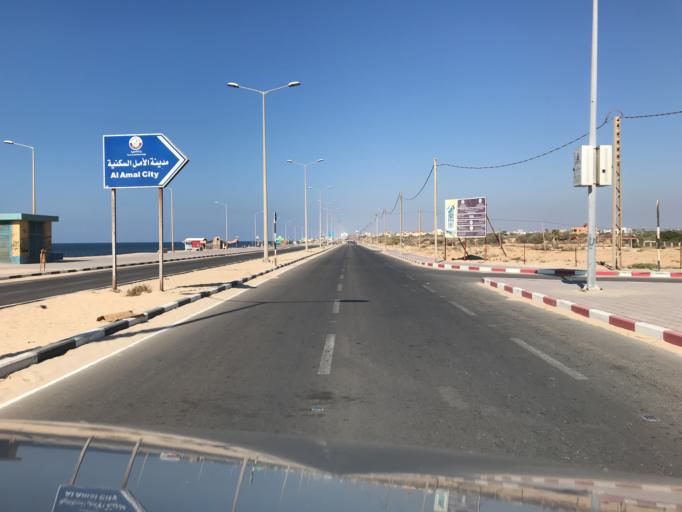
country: PS
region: Gaza Strip
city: An Nusayrat
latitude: 31.4716
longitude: 34.3838
